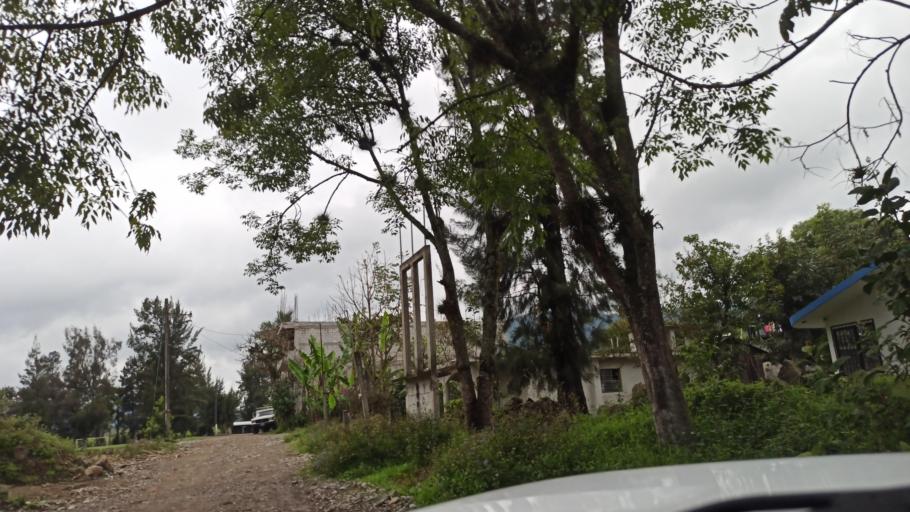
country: MX
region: Veracruz
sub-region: Chocaman
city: San Jose Neria
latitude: 18.9920
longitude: -96.9979
